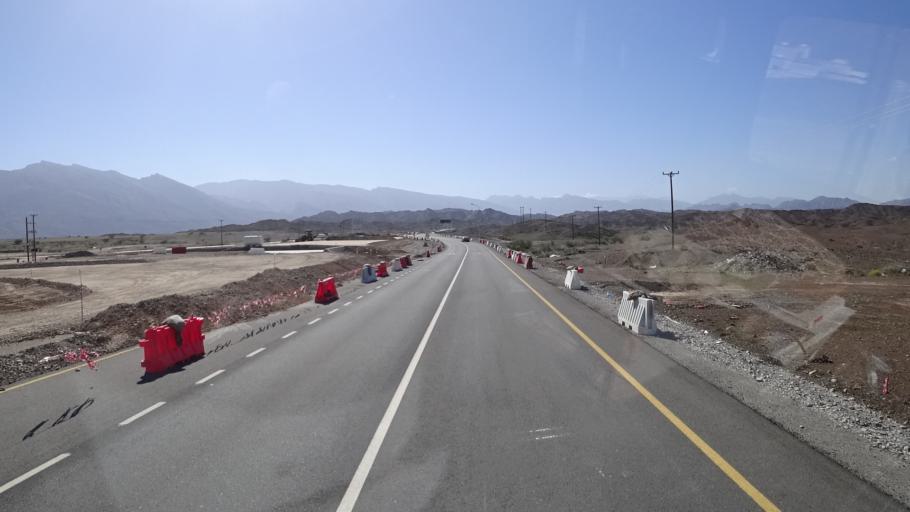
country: OM
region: Al Batinah
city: Bayt al `Awabi
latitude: 23.3748
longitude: 57.6910
